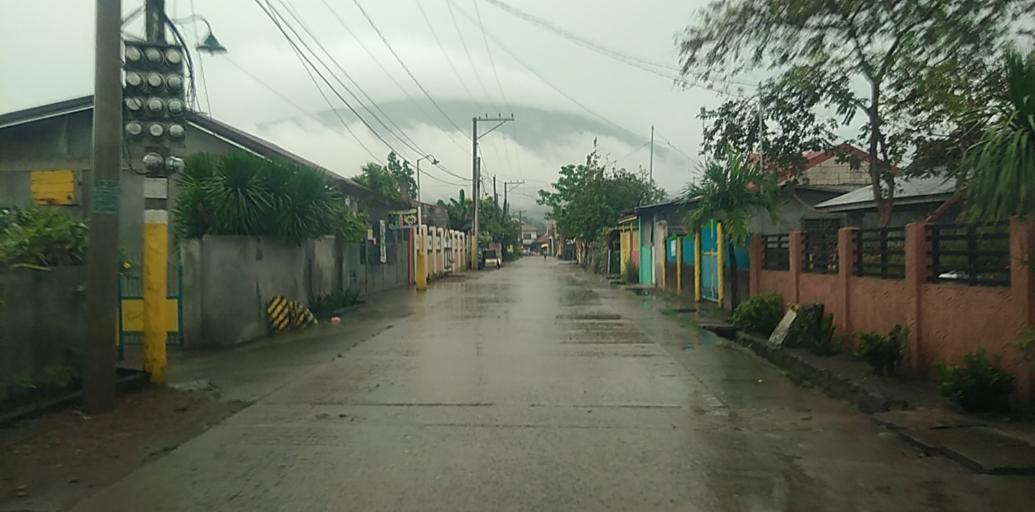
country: PH
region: Central Luzon
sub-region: Province of Pampanga
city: Anao
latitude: 15.1557
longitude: 120.7229
